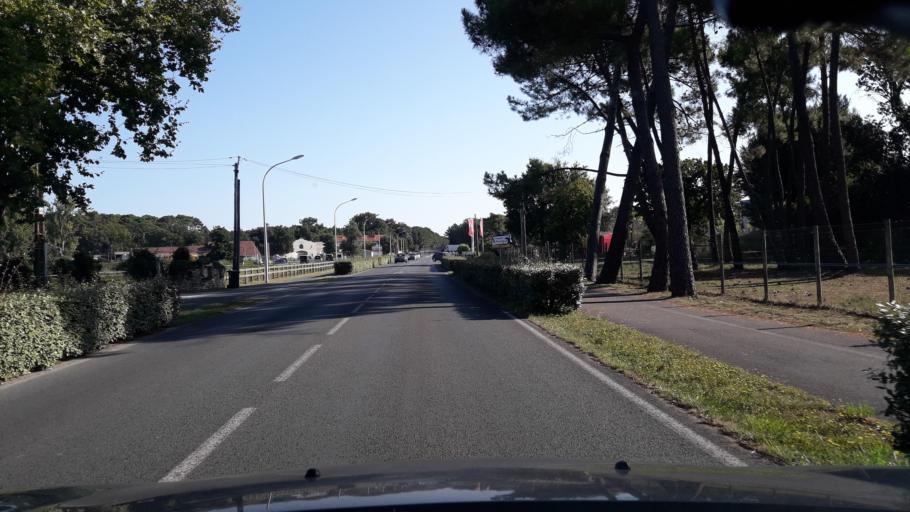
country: FR
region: Poitou-Charentes
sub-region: Departement de la Charente-Maritime
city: Les Mathes
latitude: 45.7010
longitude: -1.1700
